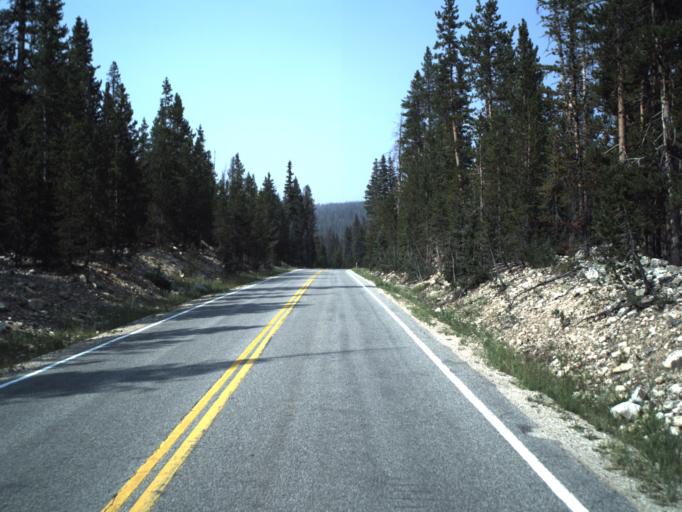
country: US
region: Utah
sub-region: Summit County
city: Kamas
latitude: 40.6453
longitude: -110.9469
